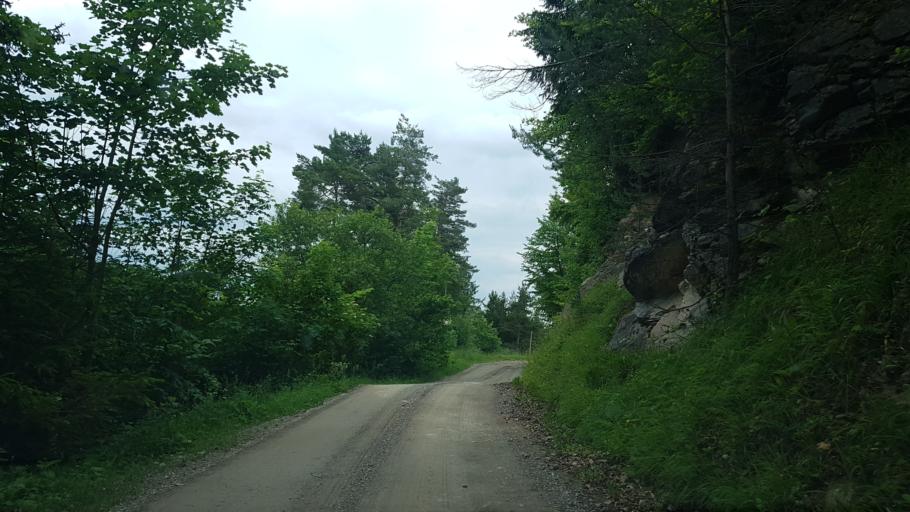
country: SI
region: Dobrna
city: Dobrna
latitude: 46.3663
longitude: 15.2458
